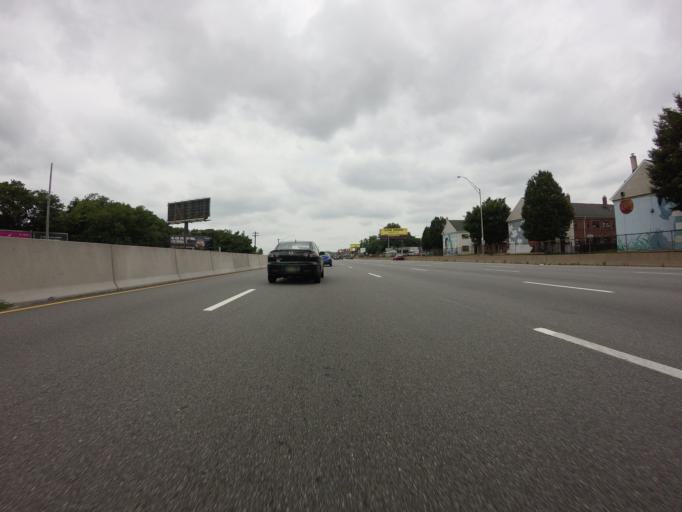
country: US
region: Pennsylvania
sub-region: Philadelphia County
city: Philadelphia
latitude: 39.9240
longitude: -75.1923
